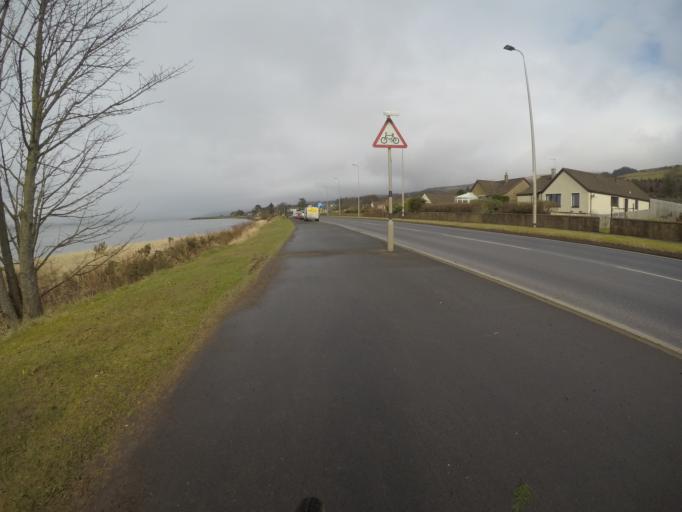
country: GB
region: Scotland
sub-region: North Ayrshire
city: Fairlie
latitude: 55.7472
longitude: -4.8571
